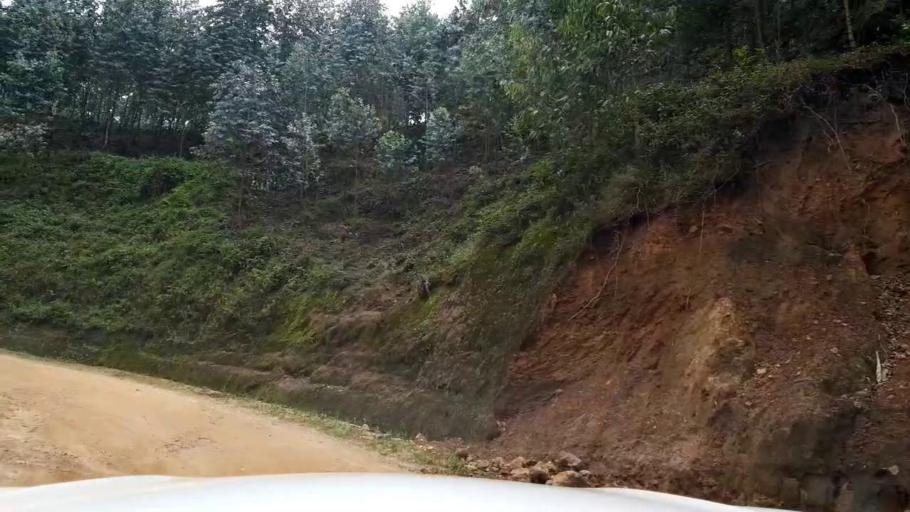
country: RW
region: Western Province
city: Kibuye
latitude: -1.9595
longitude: 29.3994
